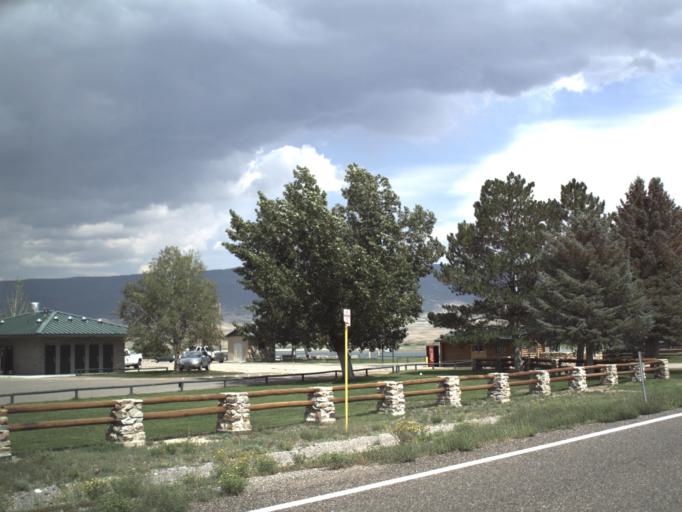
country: US
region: Utah
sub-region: Piute County
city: Junction
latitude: 38.1673
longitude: -112.0215
